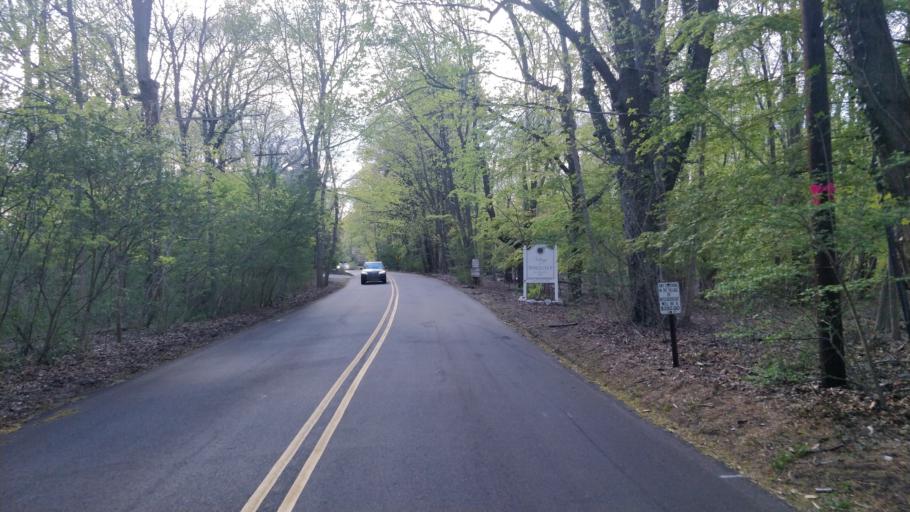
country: US
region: New York
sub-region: Suffolk County
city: Nissequogue
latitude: 40.8897
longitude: -73.1792
